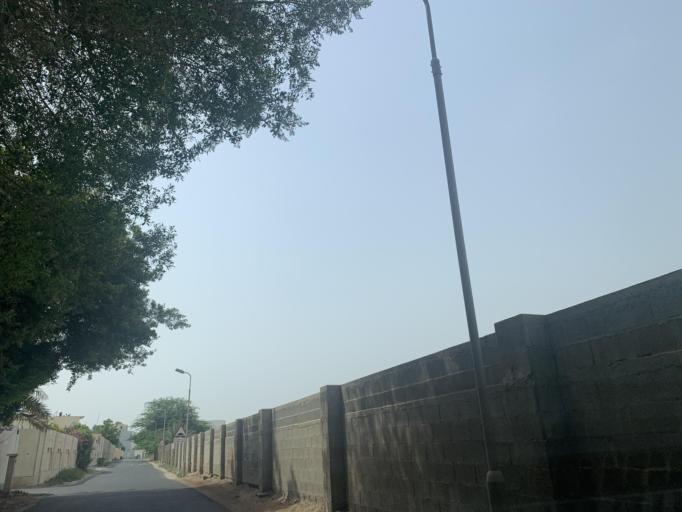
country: BH
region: Northern
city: Madinat `Isa
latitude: 26.1960
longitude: 50.4700
